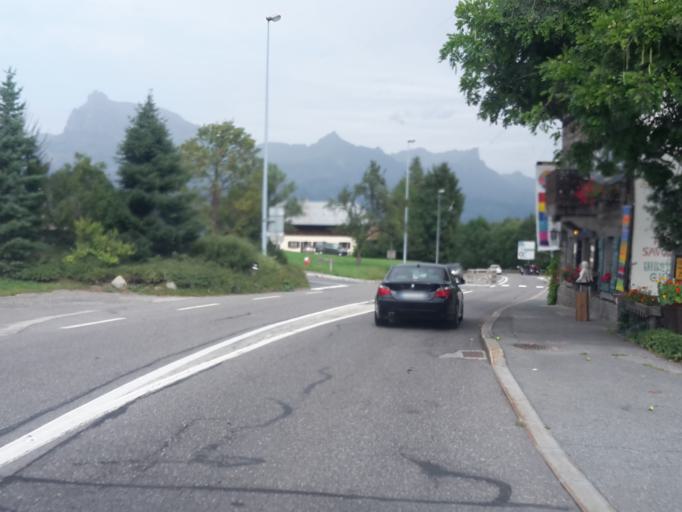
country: FR
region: Rhone-Alpes
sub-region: Departement de la Haute-Savoie
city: Combloux
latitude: 45.8799
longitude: 6.6387
